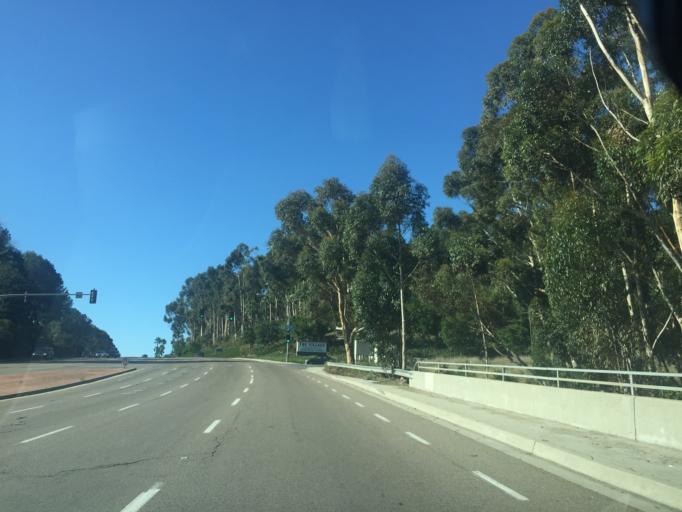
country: US
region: California
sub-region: San Diego County
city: La Mesa
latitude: 32.7906
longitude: -117.1043
